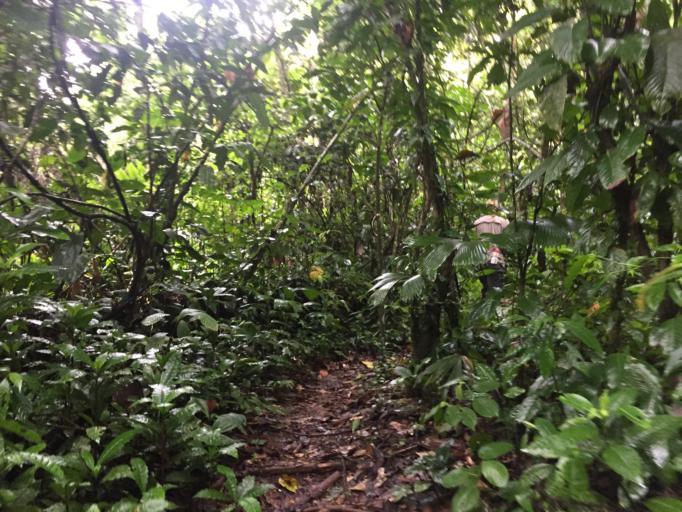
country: PE
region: Cusco
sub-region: Provincia de Paucartambo
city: Pillcopata
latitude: -12.8160
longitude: -71.4002
